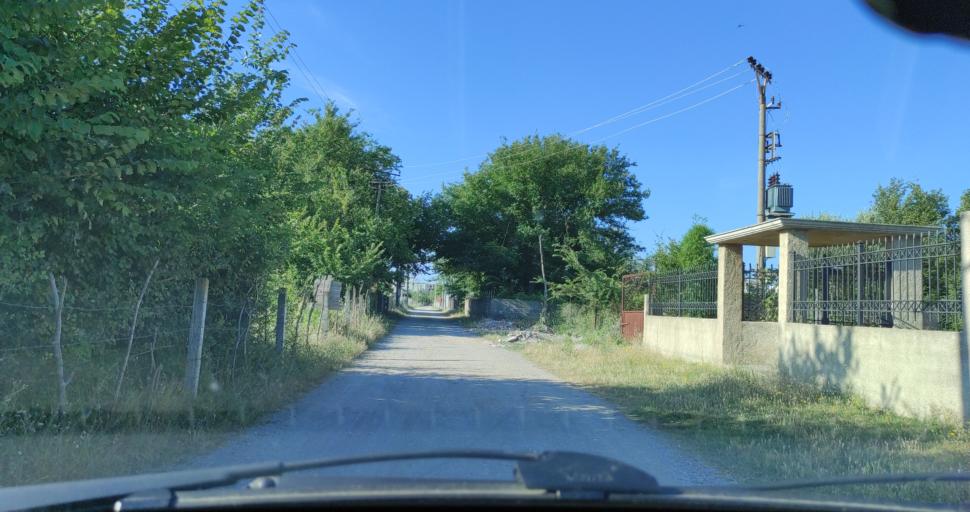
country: AL
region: Shkoder
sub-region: Rrethi i Shkodres
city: Velipoje
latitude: 41.8697
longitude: 19.4260
